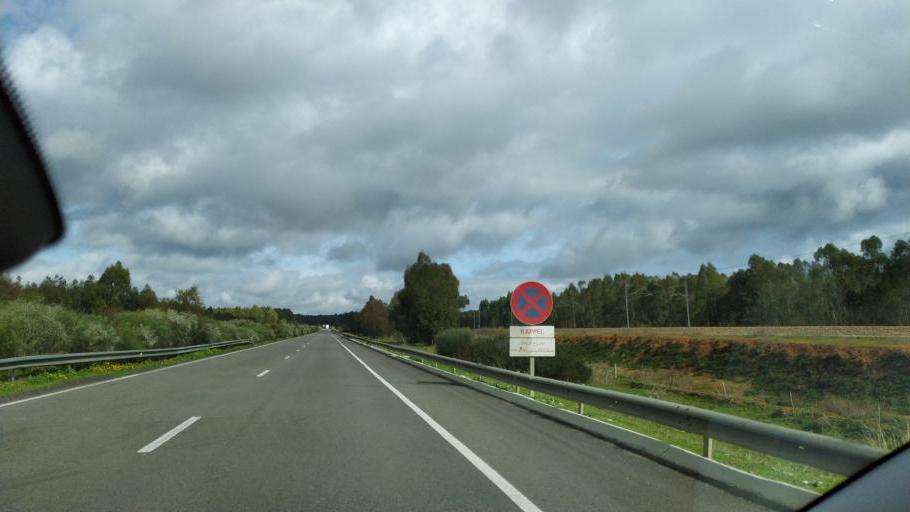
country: MA
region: Gharb-Chrarda-Beni Hssen
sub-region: Kenitra Province
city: Lalla Mimouna
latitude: 34.9086
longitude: -6.2068
